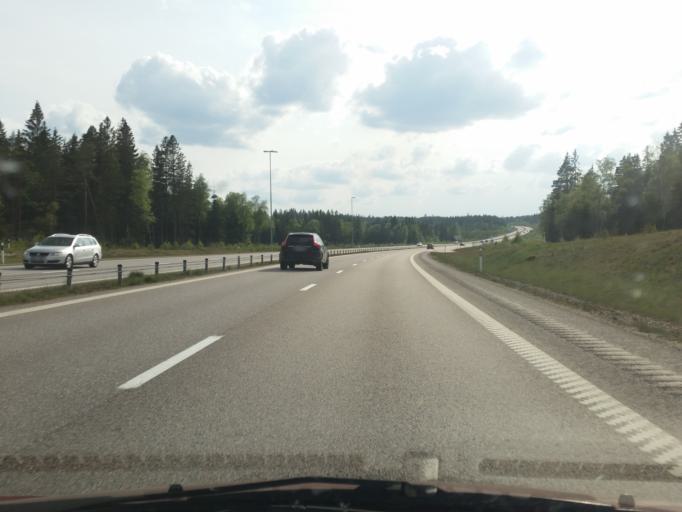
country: SE
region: Vaestra Goetaland
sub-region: Boras Kommun
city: Dalsjofors
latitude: 57.7582
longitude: 13.1017
